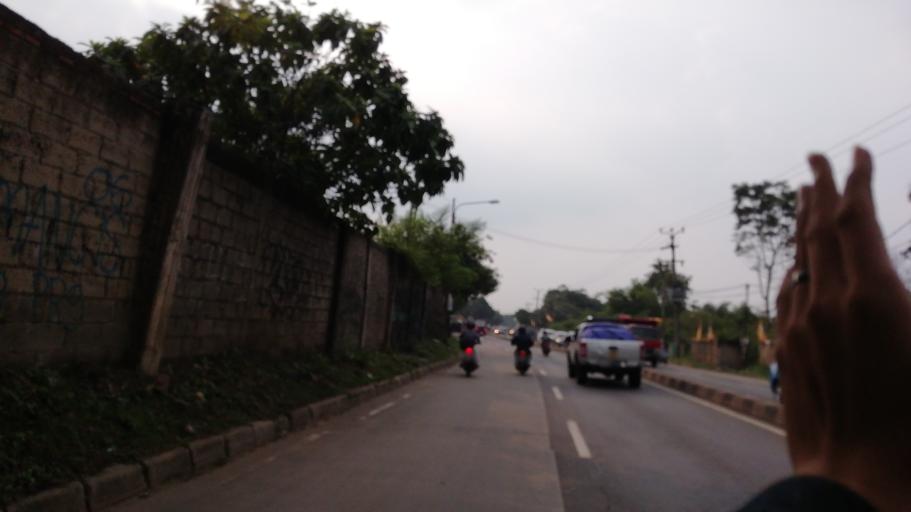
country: ID
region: West Java
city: Parung
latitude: -6.4930
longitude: 106.7454
